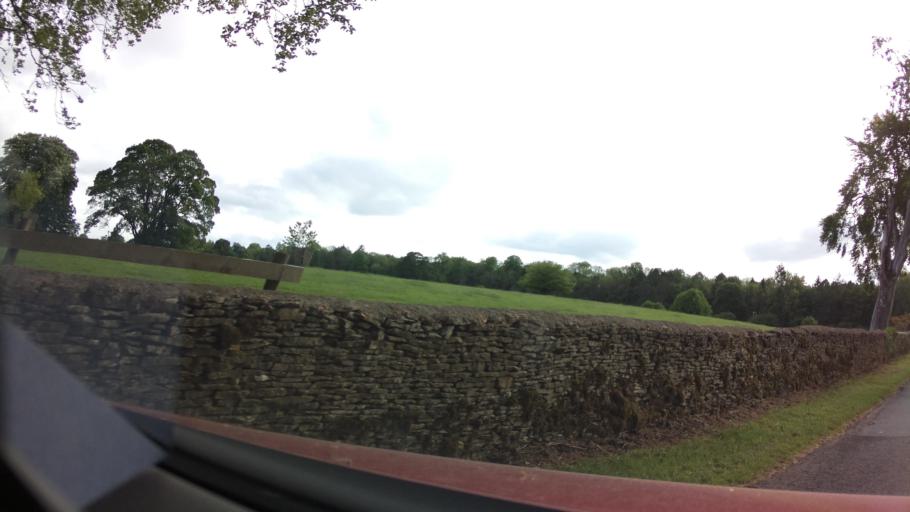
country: GB
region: England
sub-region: Gloucestershire
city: Westfield
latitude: 51.8787
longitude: -1.8978
